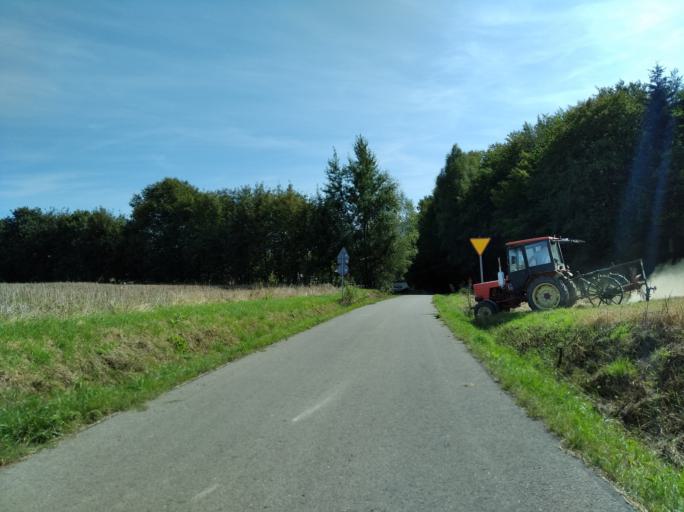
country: PL
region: Subcarpathian Voivodeship
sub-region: Powiat strzyzowski
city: Wisniowa
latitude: 49.8863
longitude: 21.6332
